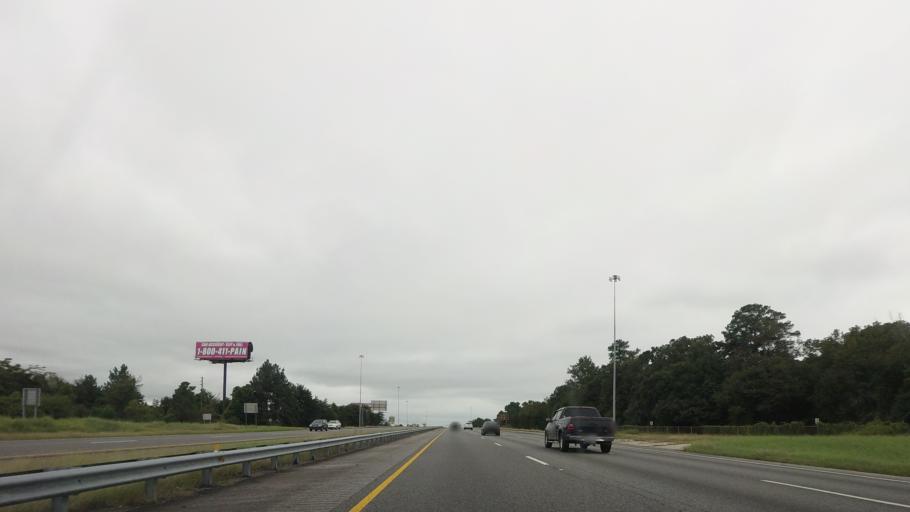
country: US
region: Georgia
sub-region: Houston County
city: Perry
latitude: 32.4455
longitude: -83.7549
